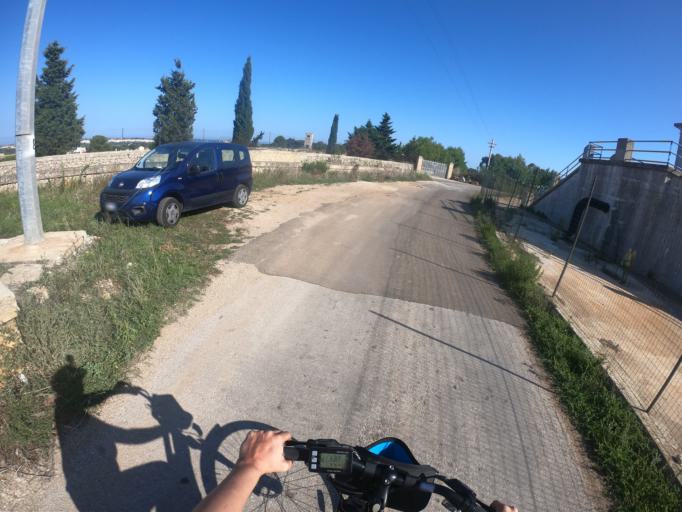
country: IT
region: Apulia
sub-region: Provincia di Lecce
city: Alessano
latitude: 39.8847
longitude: 18.3287
